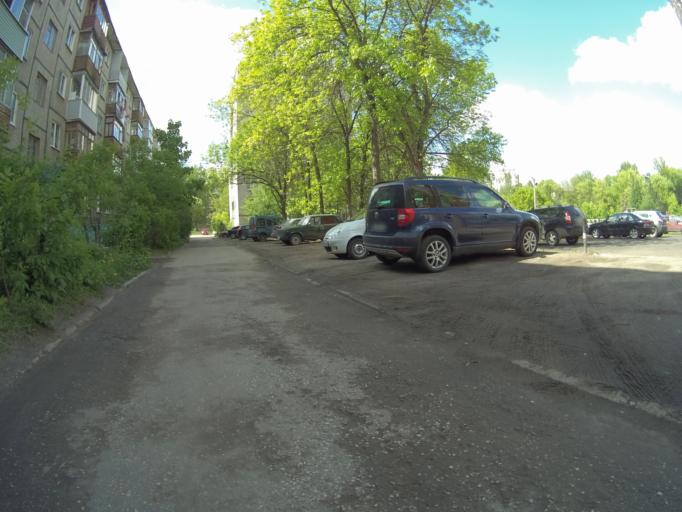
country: RU
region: Vladimir
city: Vladimir
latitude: 56.1325
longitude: 40.3543
